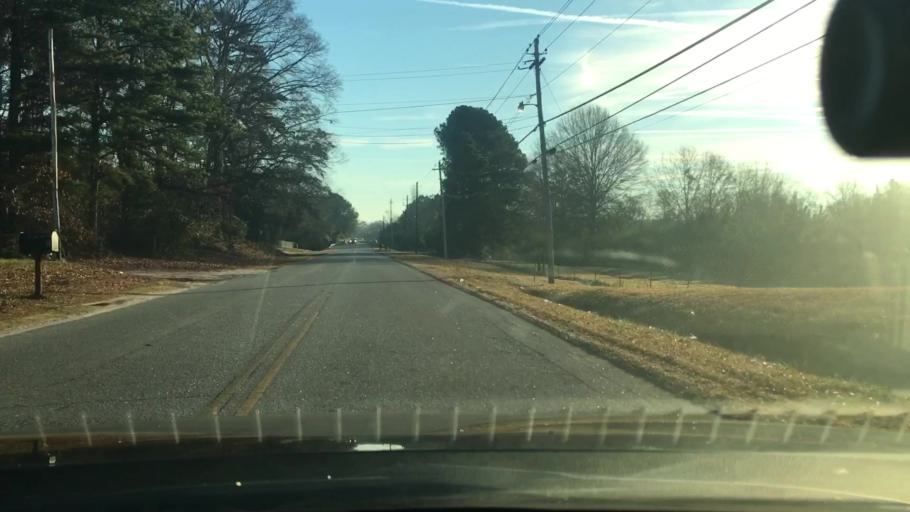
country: US
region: Georgia
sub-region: Spalding County
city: Experiment
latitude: 33.2610
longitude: -84.2943
